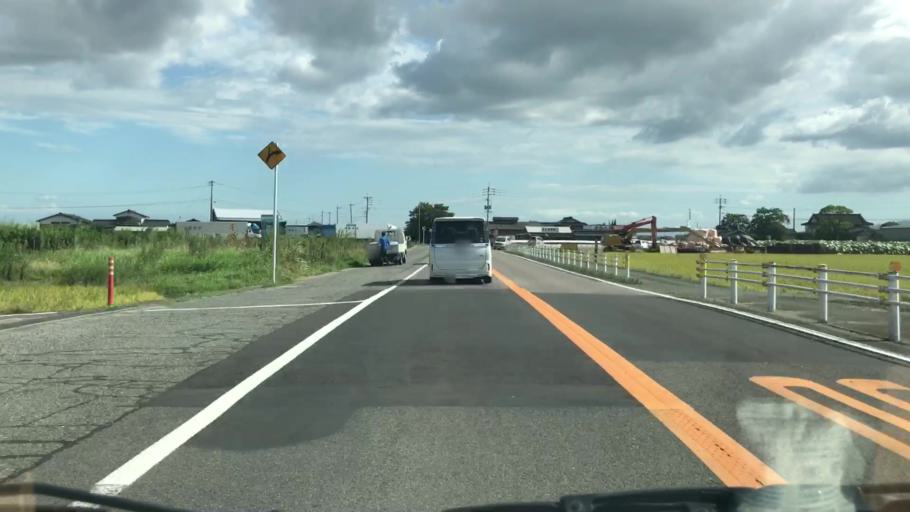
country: JP
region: Saga Prefecture
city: Kashima
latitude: 33.1714
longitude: 130.1807
